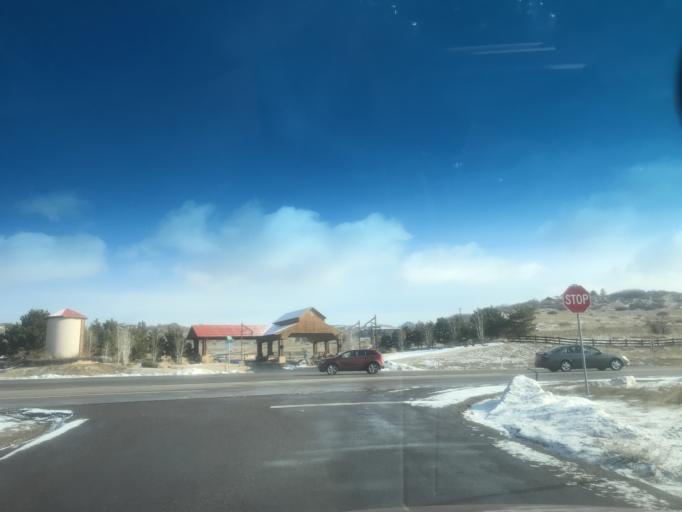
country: US
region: Colorado
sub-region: Douglas County
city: Highlands Ranch
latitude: 39.4871
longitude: -104.9964
